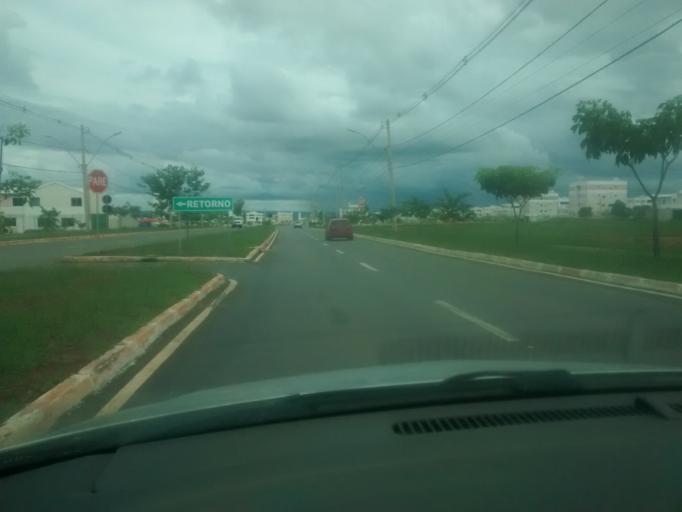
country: BR
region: Federal District
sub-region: Brasilia
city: Brasilia
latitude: -15.8893
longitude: -47.8149
